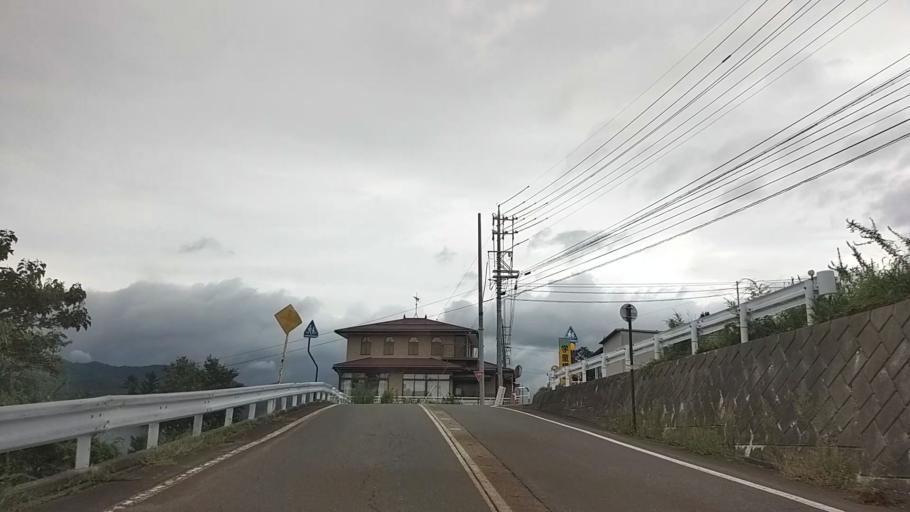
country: JP
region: Nagano
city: Iiyama
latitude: 36.8009
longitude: 138.3589
